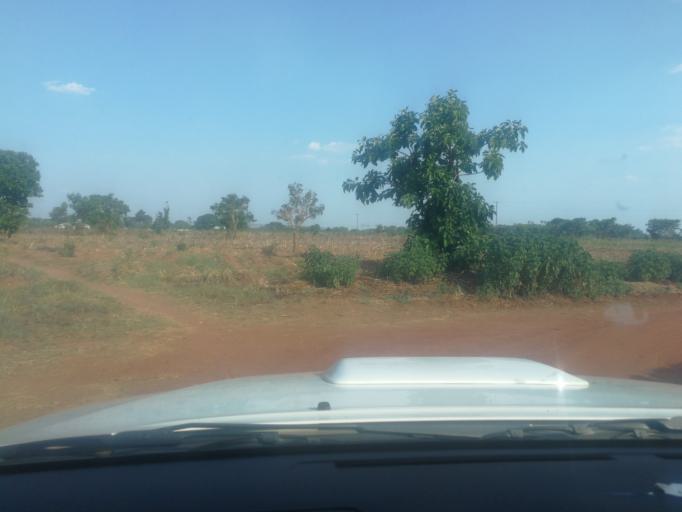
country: ZM
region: Northern
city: Kasama
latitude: -10.2157
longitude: 31.1411
